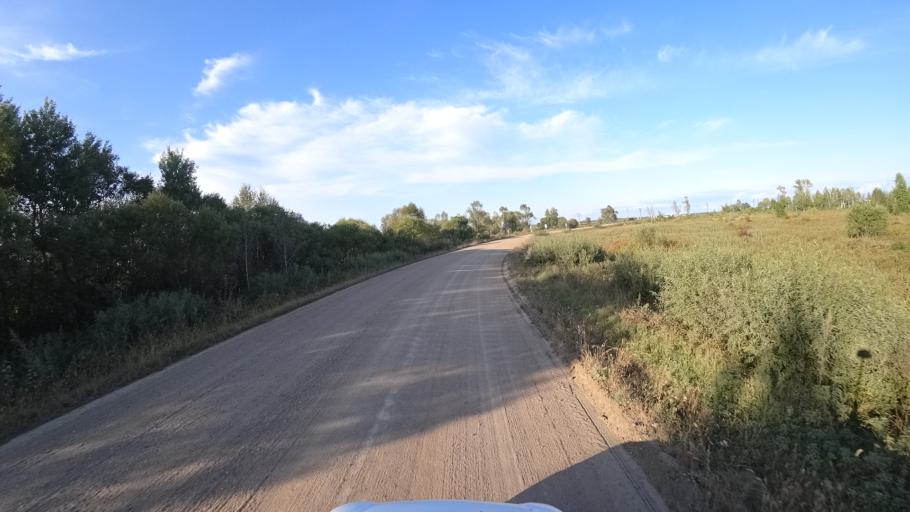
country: RU
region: Amur
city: Arkhara
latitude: 49.3687
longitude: 130.1361
